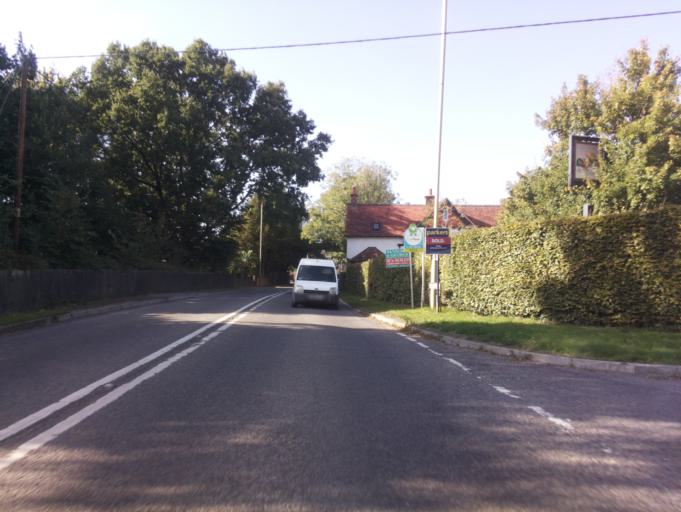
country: GB
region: England
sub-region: Hampshire
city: Tadley
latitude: 51.3408
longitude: -1.1288
